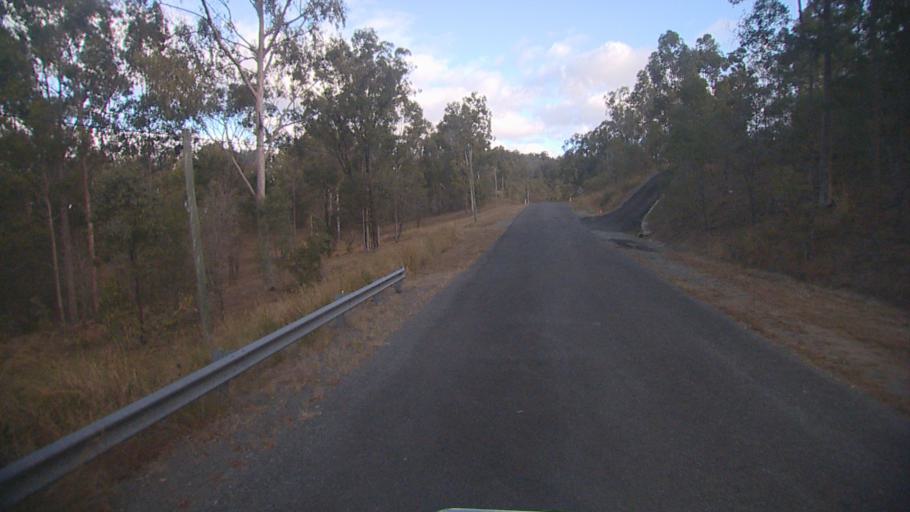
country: AU
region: Queensland
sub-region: Logan
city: Cedar Vale
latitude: -27.9024
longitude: 153.0739
